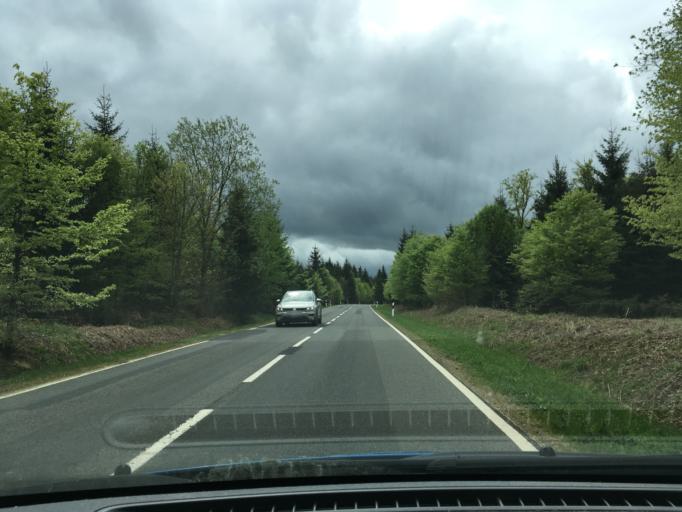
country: DE
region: Lower Saxony
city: Heinade
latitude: 51.7706
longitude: 9.5738
